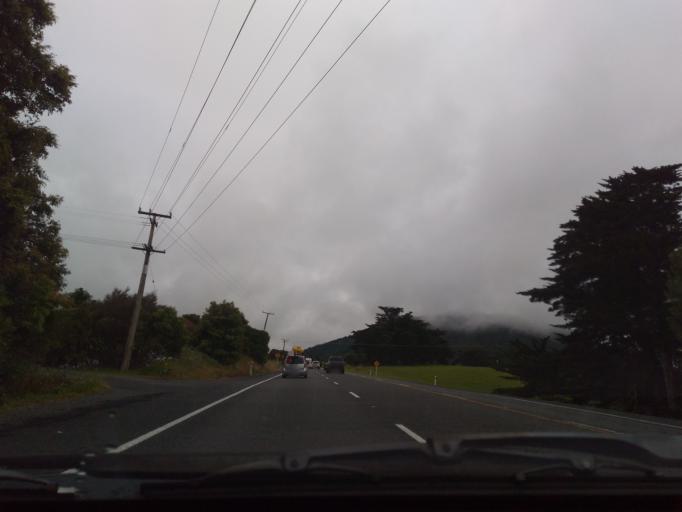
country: NZ
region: Auckland
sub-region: Auckland
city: Wellsford
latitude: -36.1489
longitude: 174.4388
